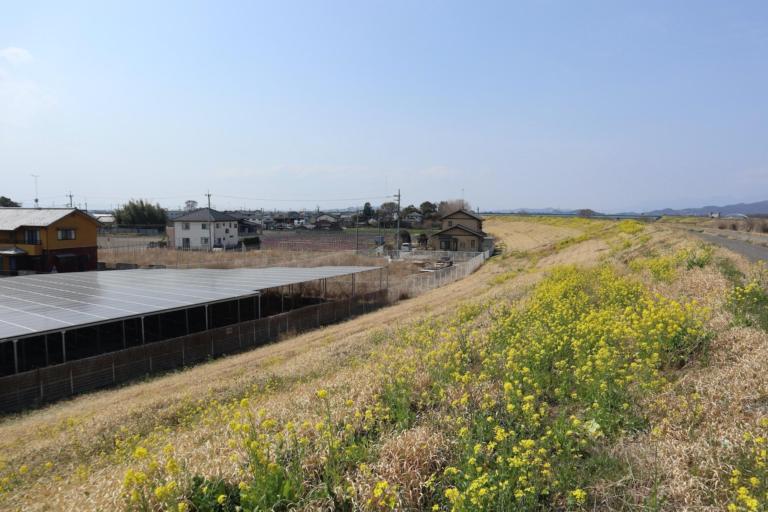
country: JP
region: Gunma
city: Tatebayashi
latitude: 36.2999
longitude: 139.5065
